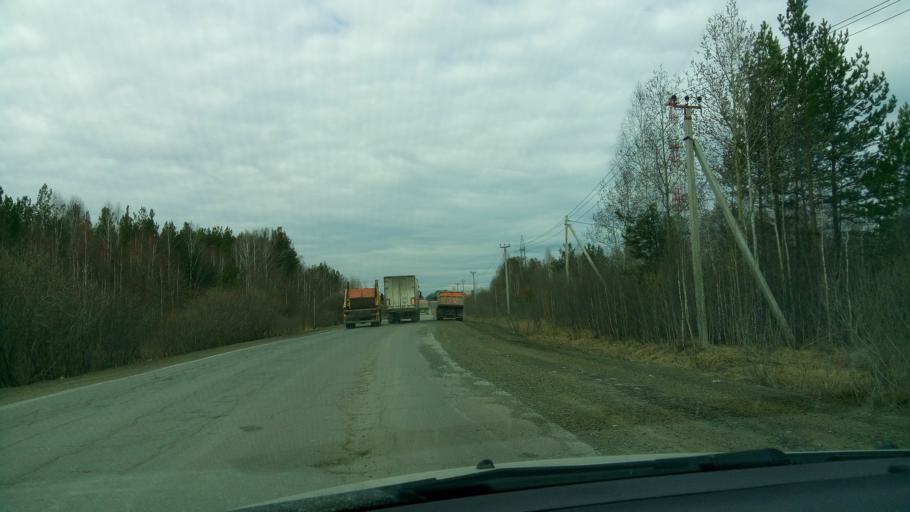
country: RU
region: Sverdlovsk
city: Verkhnyaya Pyshma
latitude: 56.9544
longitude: 60.6615
